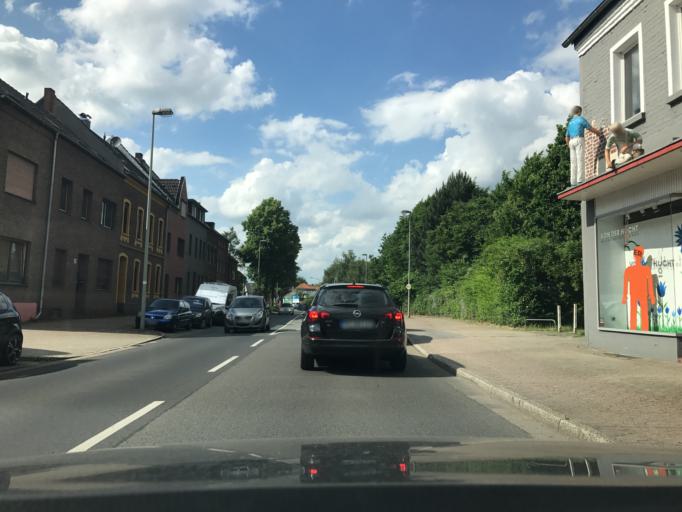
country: DE
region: North Rhine-Westphalia
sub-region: Regierungsbezirk Dusseldorf
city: Krefeld
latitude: 51.3251
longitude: 6.6166
